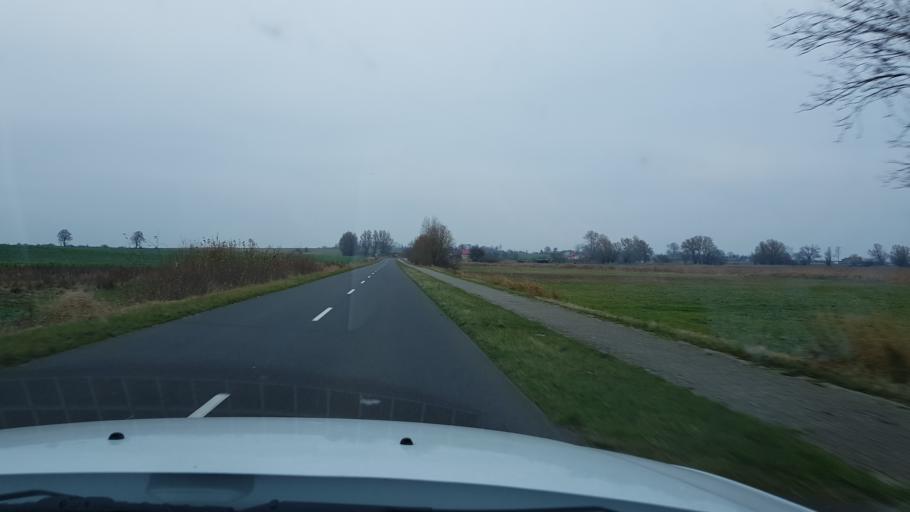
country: PL
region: West Pomeranian Voivodeship
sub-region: Powiat kamienski
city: Kamien Pomorski
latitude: 53.9706
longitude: 14.6880
